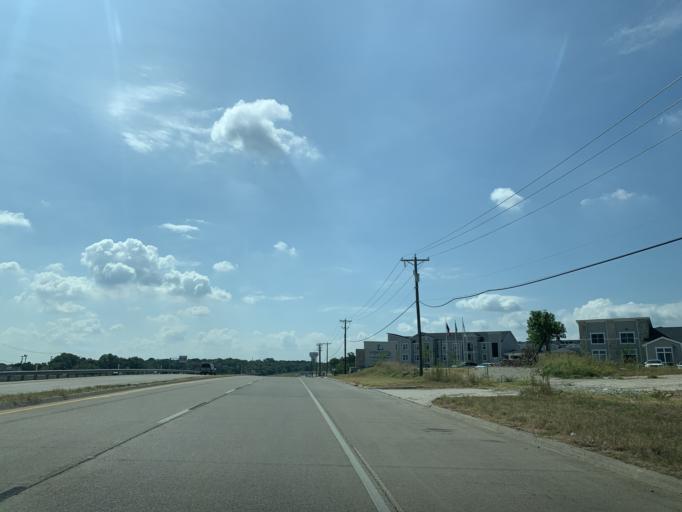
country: US
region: Texas
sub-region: Tarrant County
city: Azle
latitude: 32.8722
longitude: -97.5278
